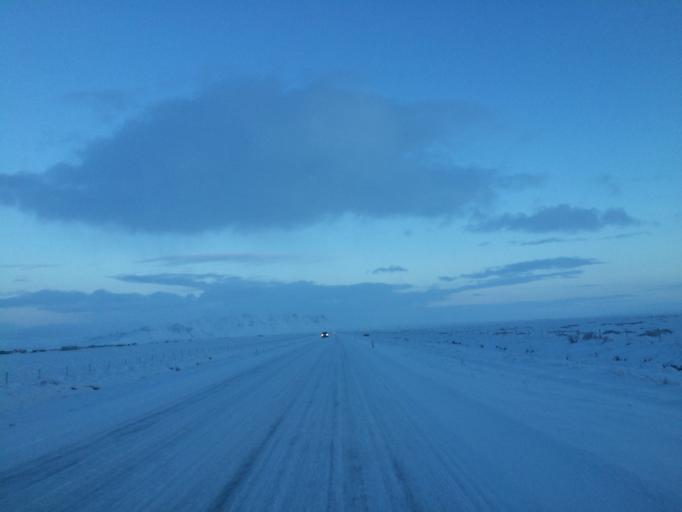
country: IS
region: South
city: Selfoss
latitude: 63.8778
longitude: -21.0910
